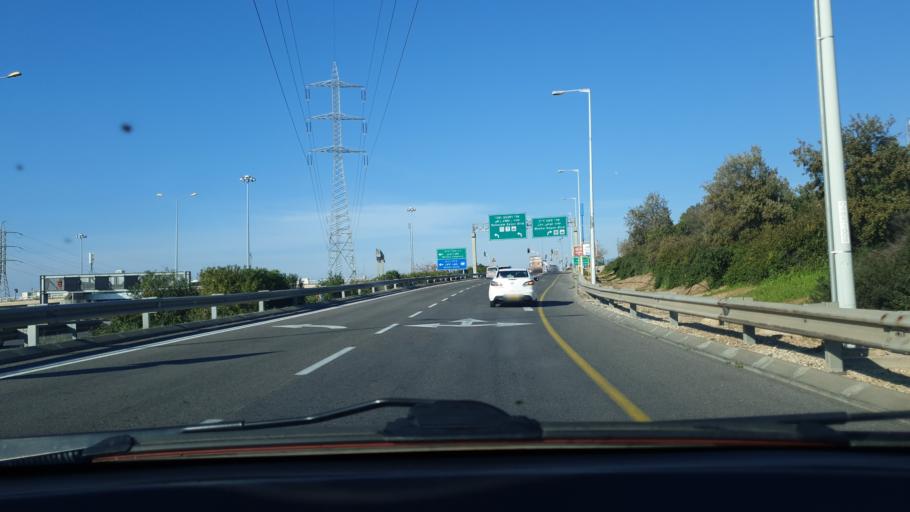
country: IL
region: Tel Aviv
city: Holon
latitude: 31.9852
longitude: 34.7575
